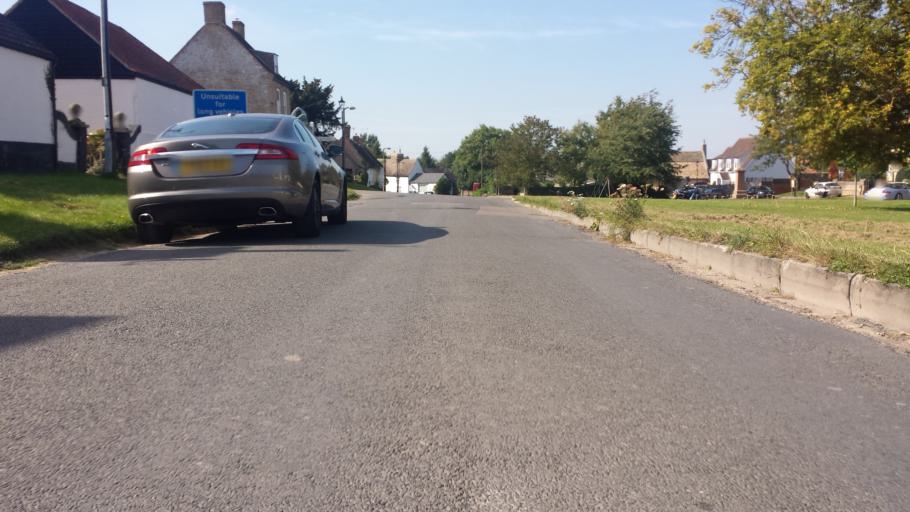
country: GB
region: England
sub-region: Cambridgeshire
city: Bottisham
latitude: 52.2710
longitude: 0.2953
